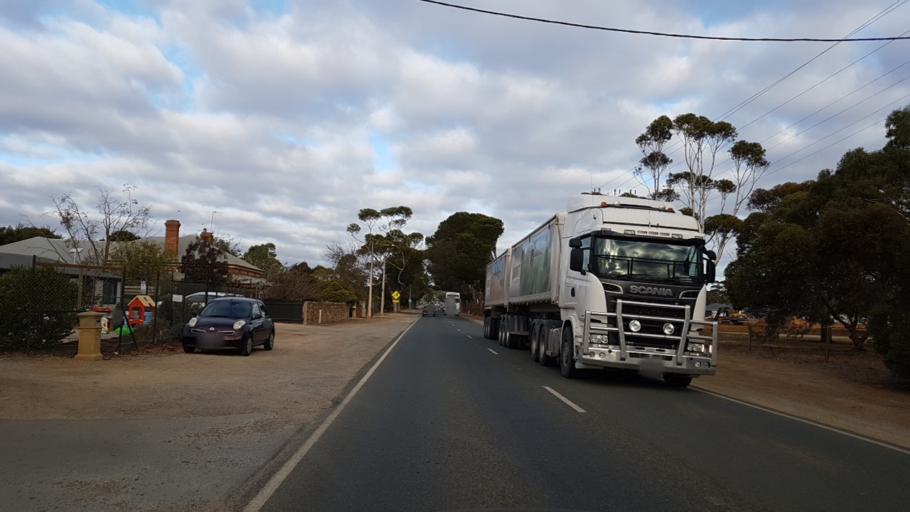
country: AU
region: South Australia
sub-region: Alexandrina
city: Strathalbyn
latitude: -35.2558
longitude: 138.9045
